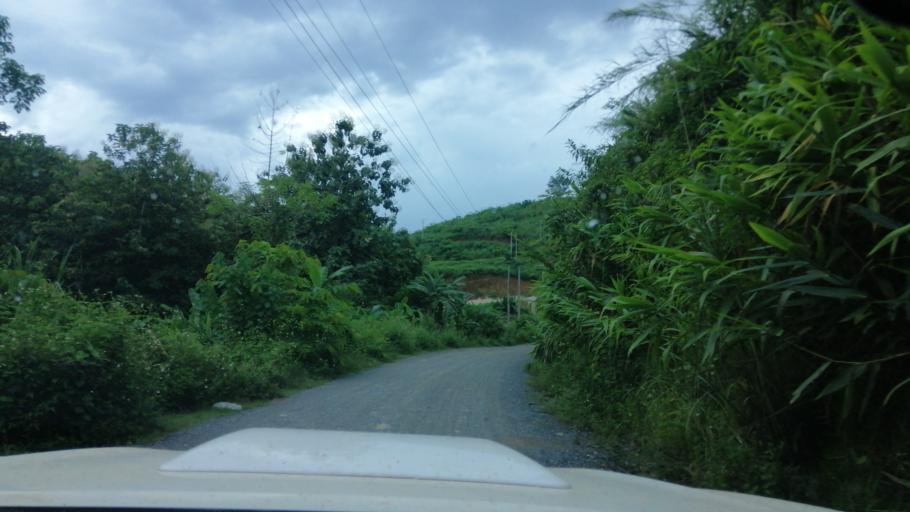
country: LA
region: Xiagnabouli
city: Sainyabuli
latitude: 19.1941
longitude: 101.7823
